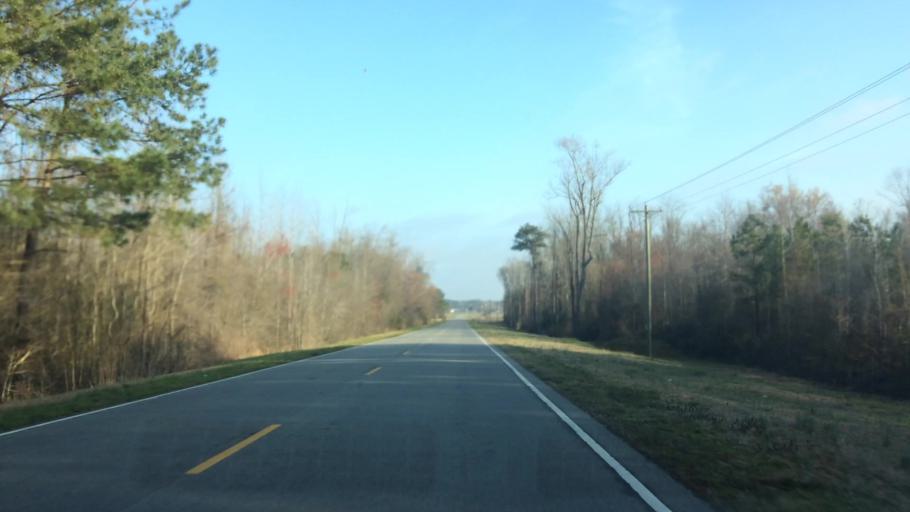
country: US
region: North Carolina
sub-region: Edgecombe County
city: Pinetops
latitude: 35.7176
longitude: -77.6339
